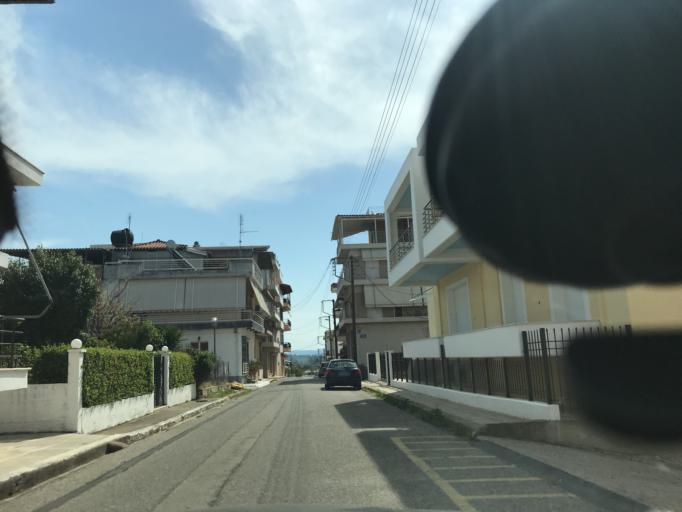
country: GR
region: West Greece
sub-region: Nomos Ileias
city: Pyrgos
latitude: 37.6727
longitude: 21.4477
